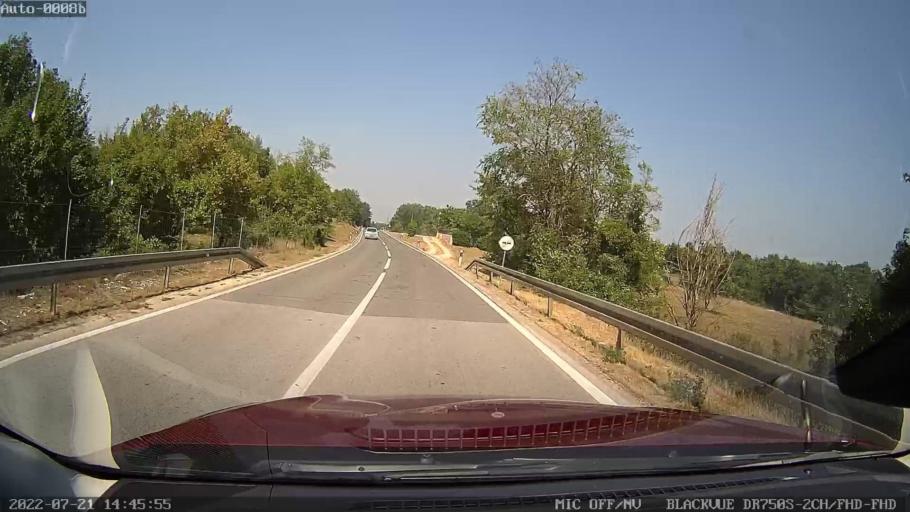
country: HR
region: Istarska
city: Pazin
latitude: 45.1324
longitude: 13.8961
